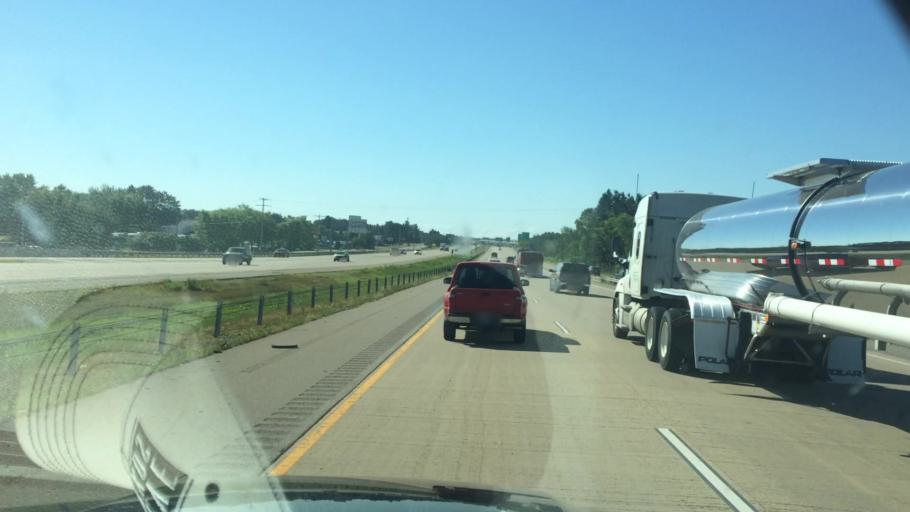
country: US
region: Wisconsin
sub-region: Marathon County
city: Rib Mountain
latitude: 44.9101
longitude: -89.6499
